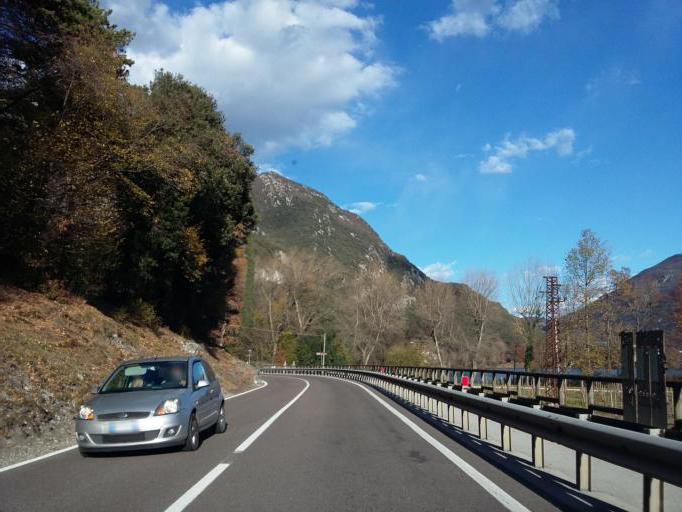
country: IT
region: Trentino-Alto Adige
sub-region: Provincia di Trento
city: Calavino
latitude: 46.0511
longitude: 10.9579
